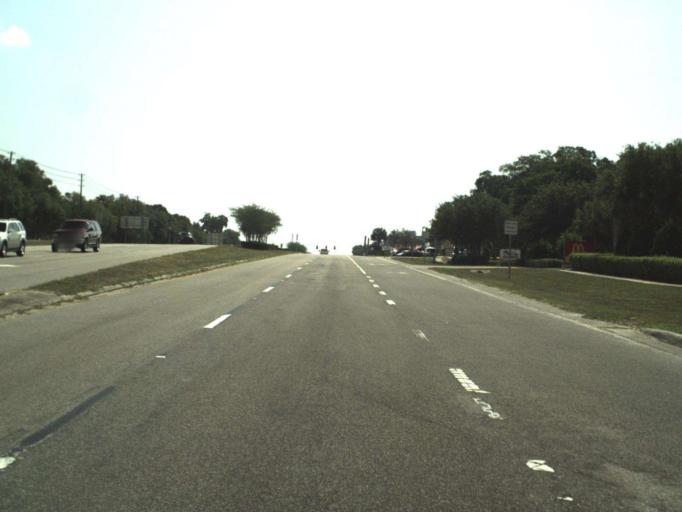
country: US
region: Florida
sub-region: Volusia County
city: North DeLand
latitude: 29.0547
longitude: -81.3040
